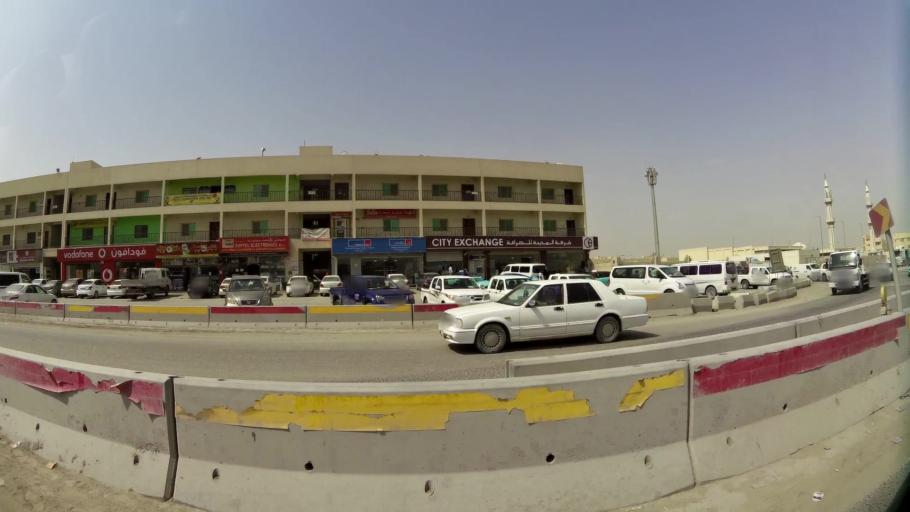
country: QA
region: Baladiyat ar Rayyan
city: Ar Rayyan
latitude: 25.1938
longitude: 51.4328
